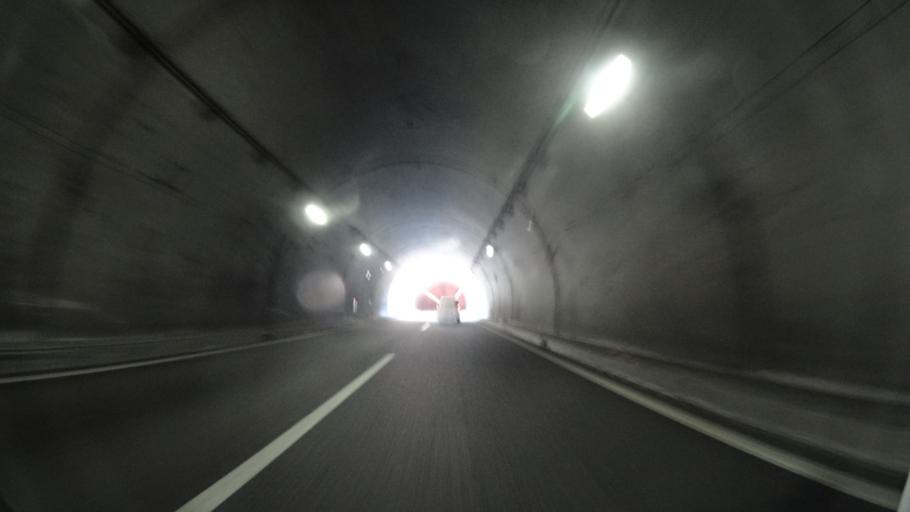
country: JP
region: Ehime
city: Saijo
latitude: 33.8863
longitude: 133.1512
